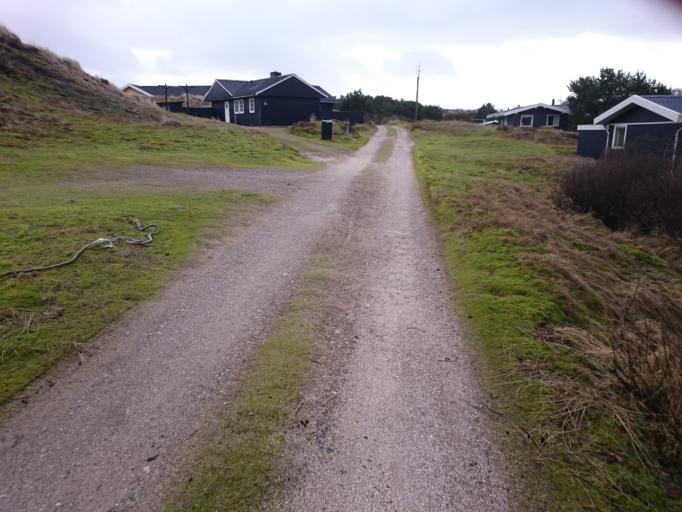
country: DK
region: South Denmark
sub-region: Fano Kommune
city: Nordby
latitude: 55.4346
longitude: 8.3794
